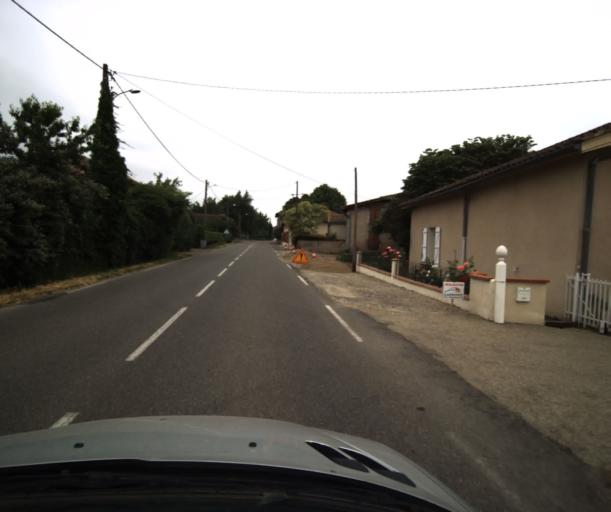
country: FR
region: Midi-Pyrenees
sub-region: Departement du Tarn-et-Garonne
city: Saint-Nicolas-de-la-Grave
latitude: 44.0603
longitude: 1.0247
